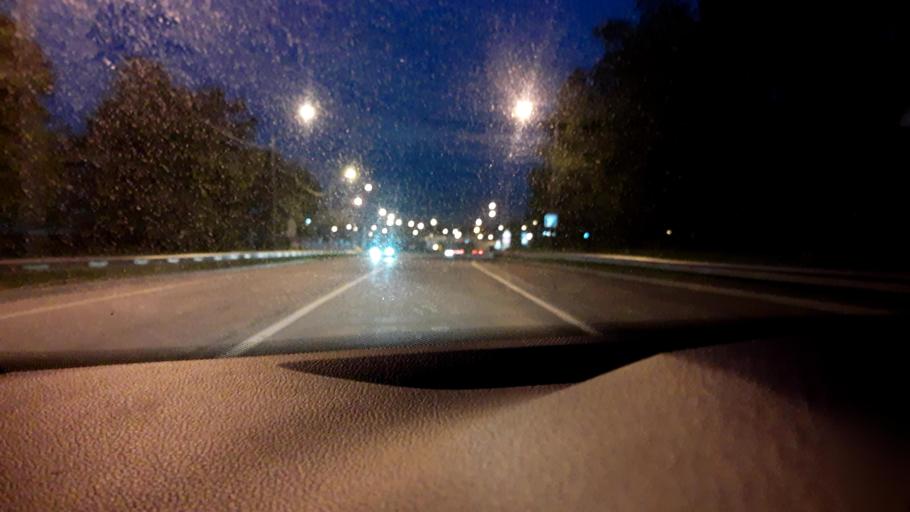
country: RU
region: Moskovskaya
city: Opalikha
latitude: 55.7848
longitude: 37.2331
